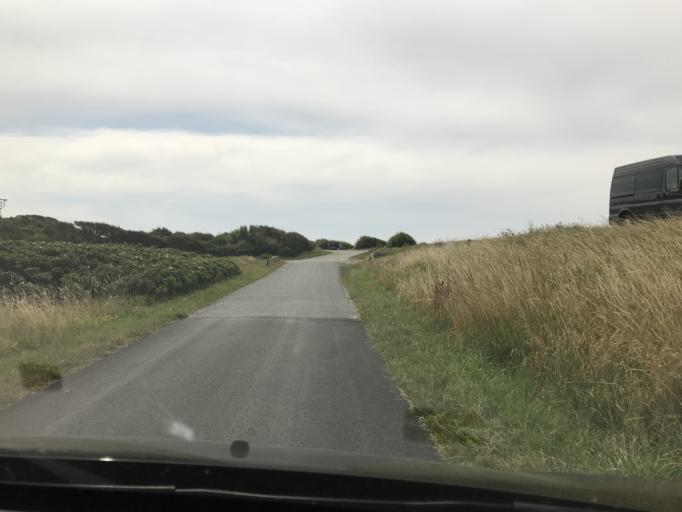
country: DK
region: South Denmark
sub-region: AEro Kommune
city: AEroskobing
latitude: 54.9233
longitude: 10.2445
